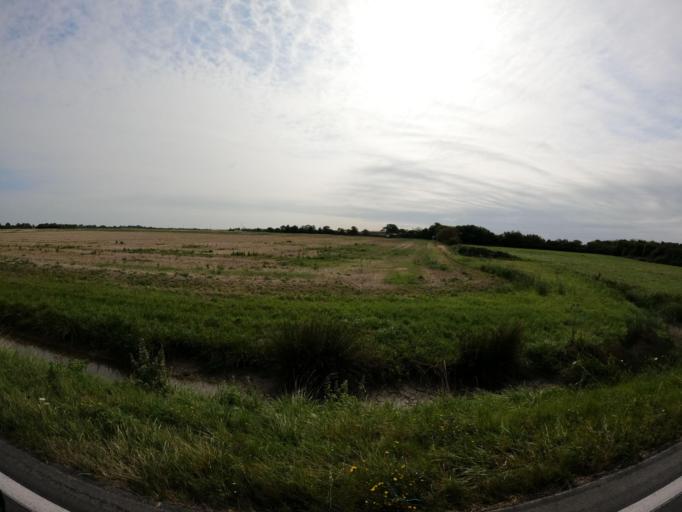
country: FR
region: Pays de la Loire
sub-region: Departement de la Vendee
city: Triaize
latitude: 46.3760
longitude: -1.2034
